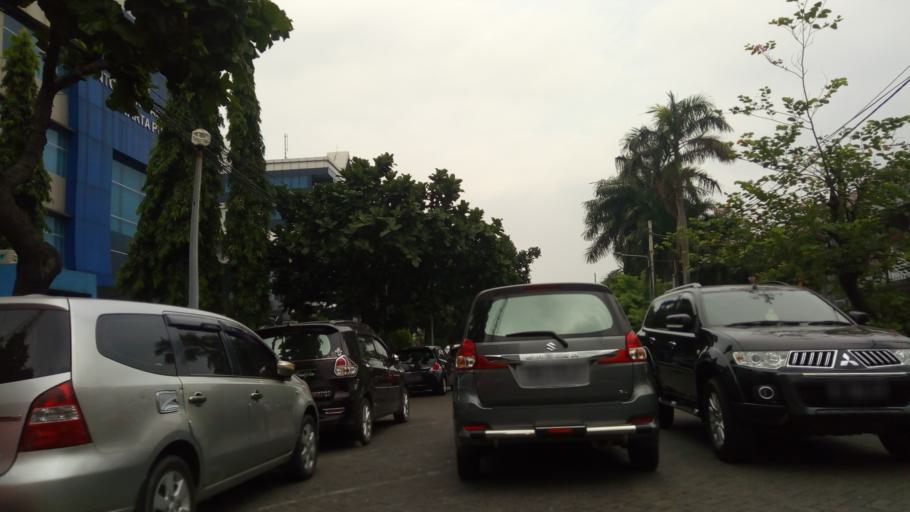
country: ID
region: Jakarta Raya
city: Jakarta
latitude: -6.1534
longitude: 106.8423
